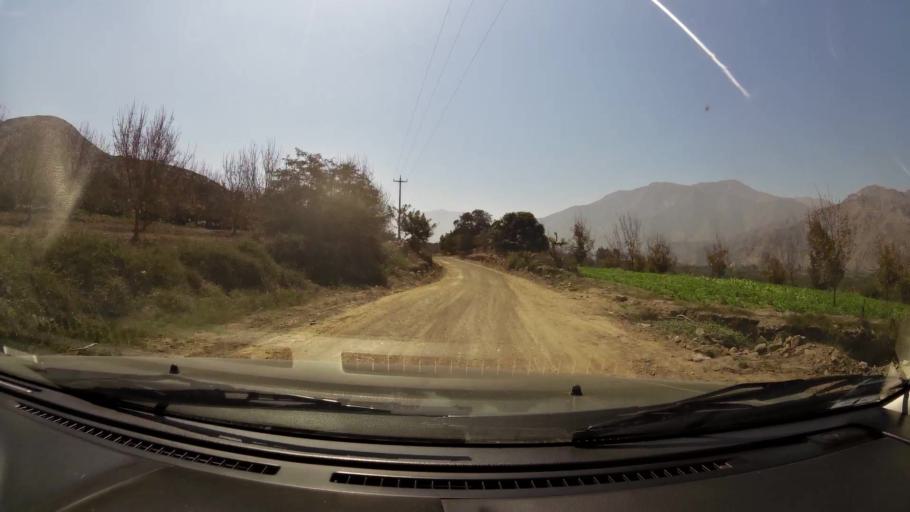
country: PE
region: Ica
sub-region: Provincia de Ica
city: Guadalupe
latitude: -13.8859
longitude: -75.6521
